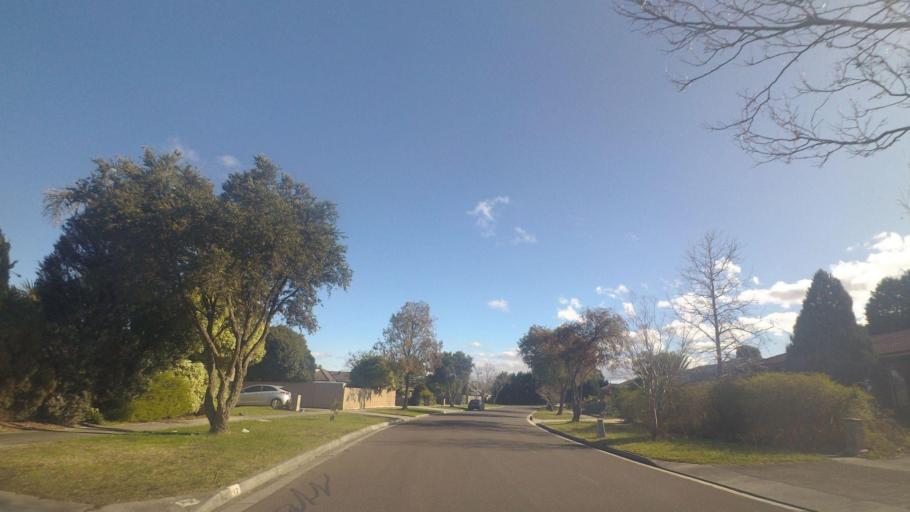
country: AU
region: Victoria
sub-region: Knox
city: Rowville
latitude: -37.9168
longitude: 145.2525
